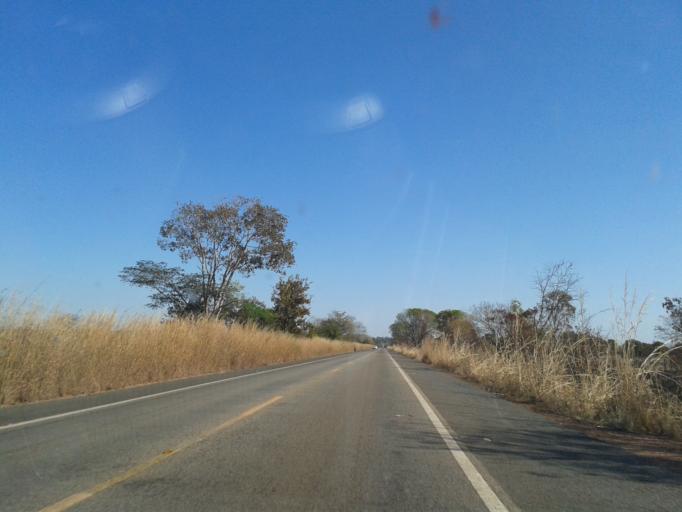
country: BR
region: Goias
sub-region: Mozarlandia
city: Mozarlandia
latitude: -15.0527
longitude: -50.6103
